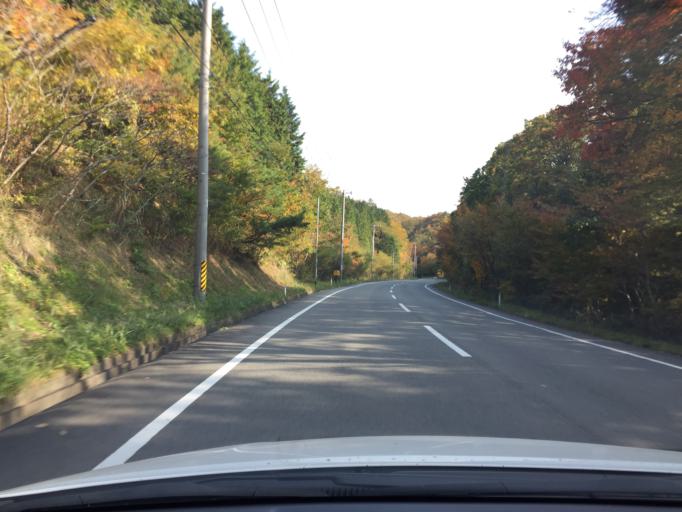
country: JP
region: Ibaraki
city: Kitaibaraki
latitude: 36.9593
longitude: 140.6012
